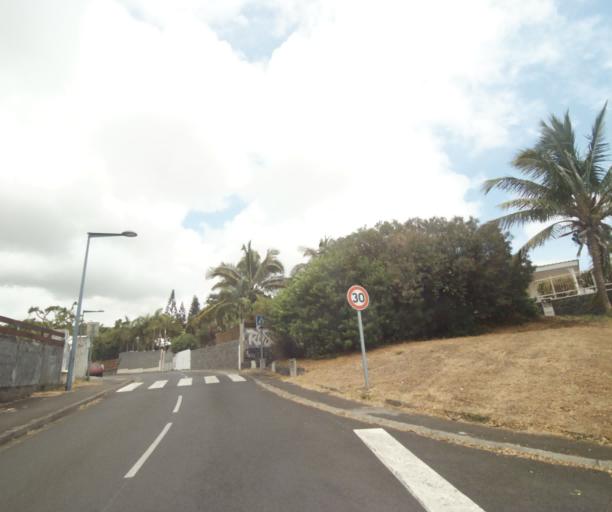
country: RE
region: Reunion
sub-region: Reunion
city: Saint-Paul
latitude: -21.0264
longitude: 55.2714
